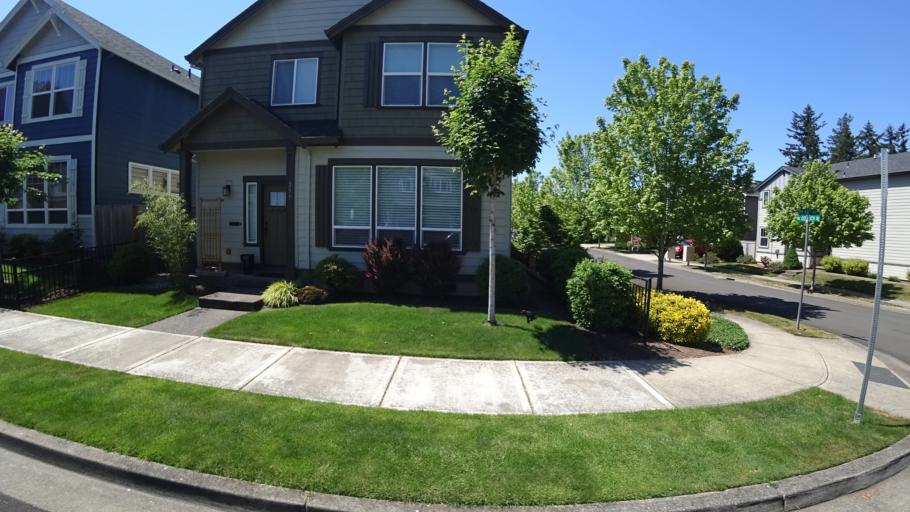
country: US
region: Oregon
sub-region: Washington County
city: Rockcreek
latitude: 45.5238
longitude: -122.9131
